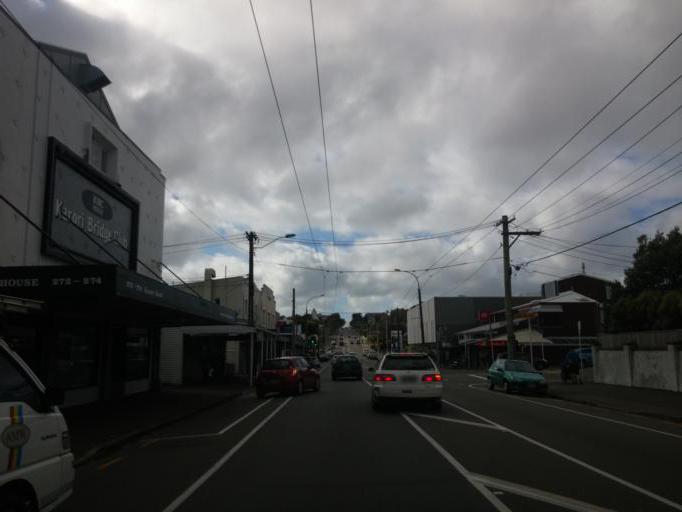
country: NZ
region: Wellington
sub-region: Wellington City
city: Kelburn
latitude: -41.2850
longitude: 174.7364
